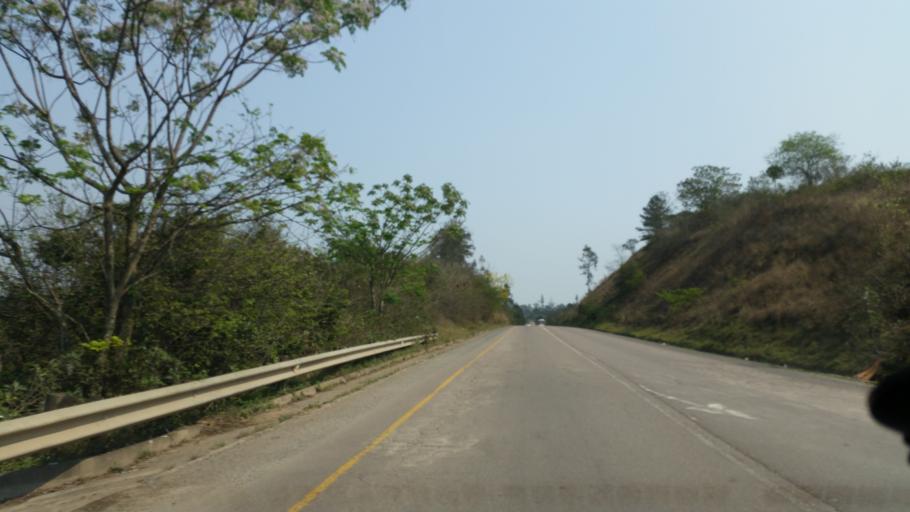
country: ZA
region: KwaZulu-Natal
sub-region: eThekwini Metropolitan Municipality
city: Mpumalanga
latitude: -29.7371
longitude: 30.6575
